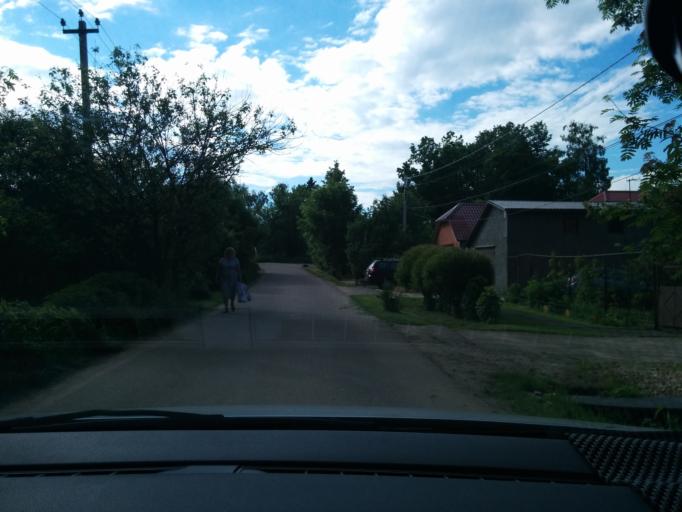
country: RU
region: Moskovskaya
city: Lugovaya
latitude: 56.0535
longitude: 37.4795
